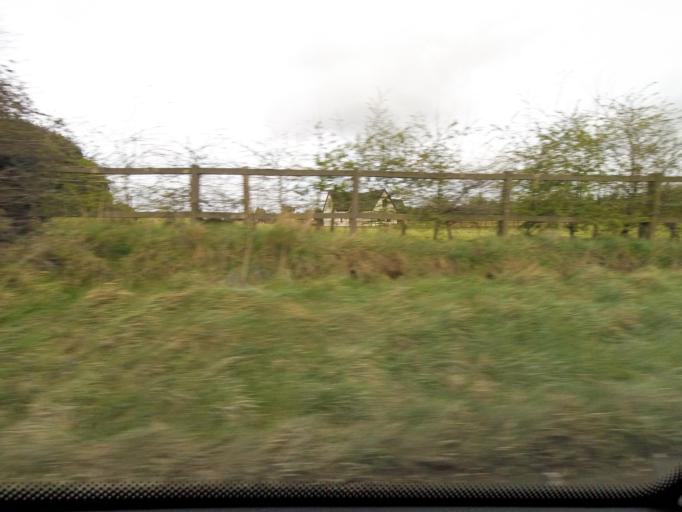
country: IE
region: Leinster
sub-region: Kildare
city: Johnstown
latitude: 53.2016
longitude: -6.6223
